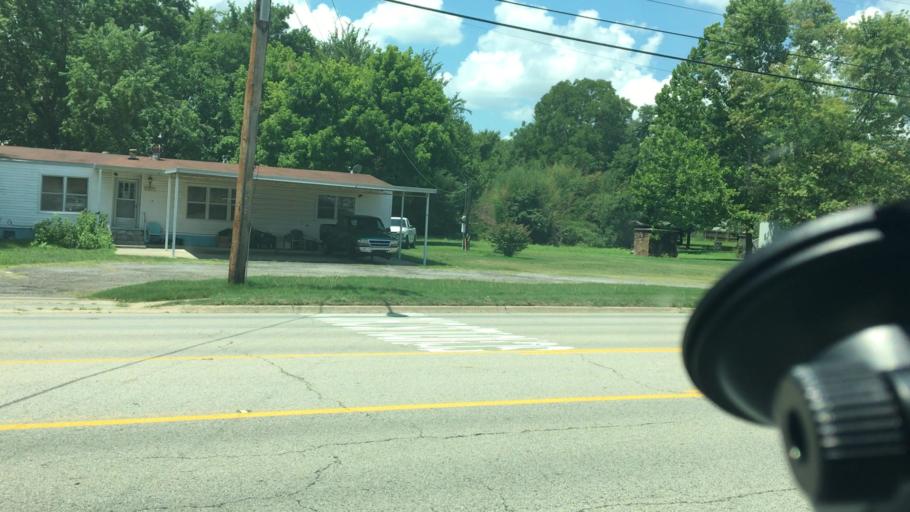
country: US
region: Arkansas
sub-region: Sebastian County
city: Barling
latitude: 35.3306
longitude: -94.3077
